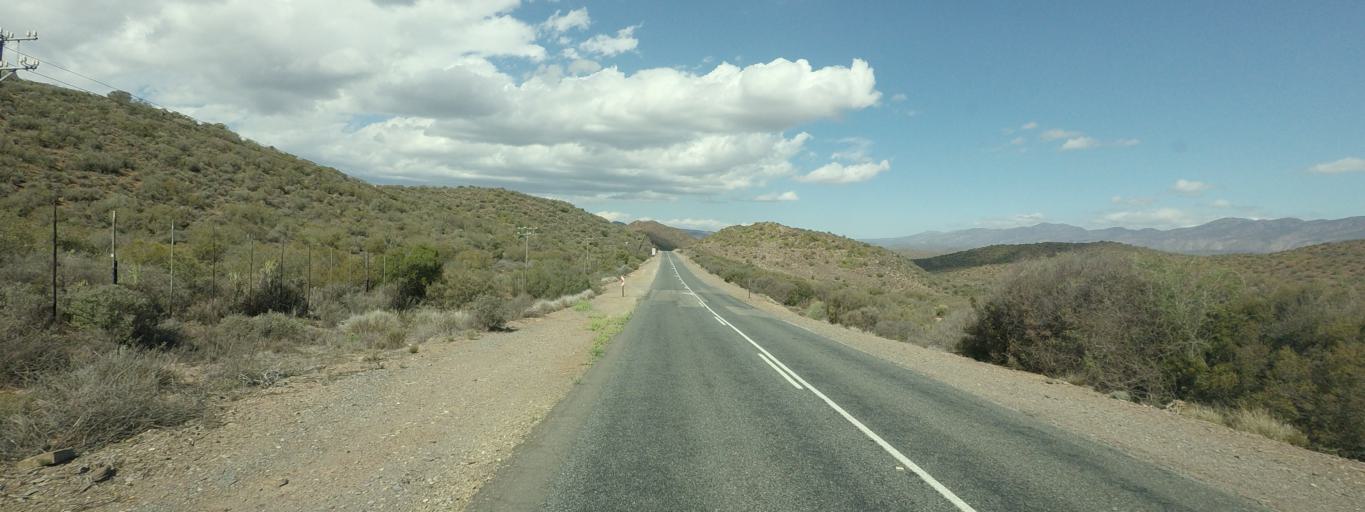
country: ZA
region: Western Cape
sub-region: Eden District Municipality
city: Ladismith
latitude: -33.5386
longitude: 21.2410
